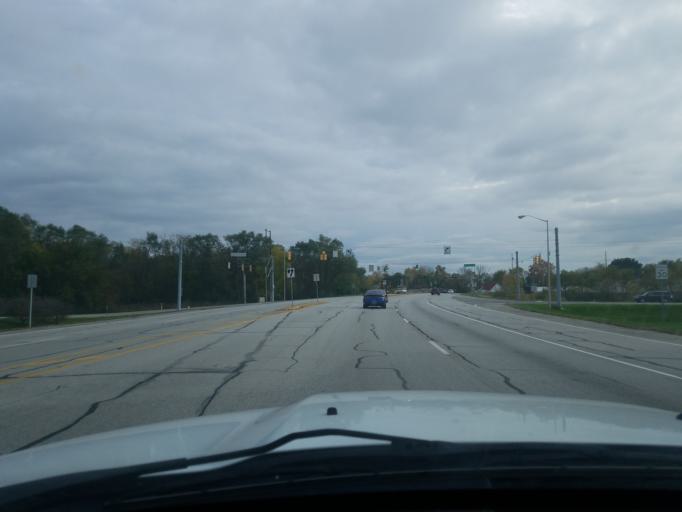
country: US
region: Indiana
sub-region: Shelby County
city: Shelbyville
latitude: 39.5326
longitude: -85.7771
